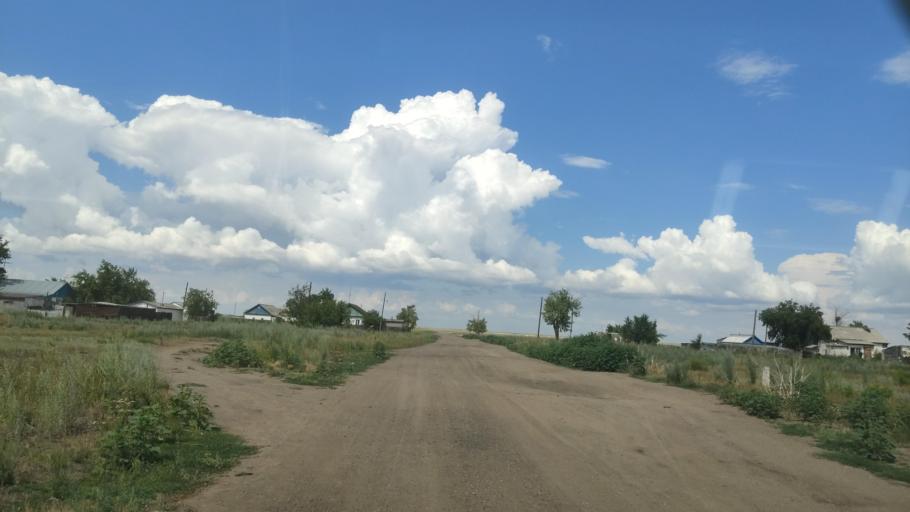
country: KZ
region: Pavlodar
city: Pavlodar
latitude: 52.6218
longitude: 77.2058
